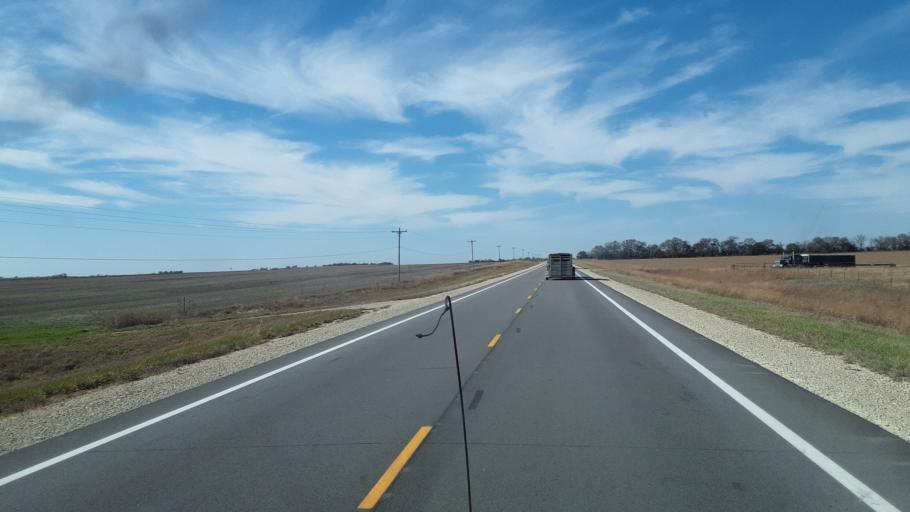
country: US
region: Kansas
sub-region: Marion County
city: Marion
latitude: 38.3629
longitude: -96.9153
